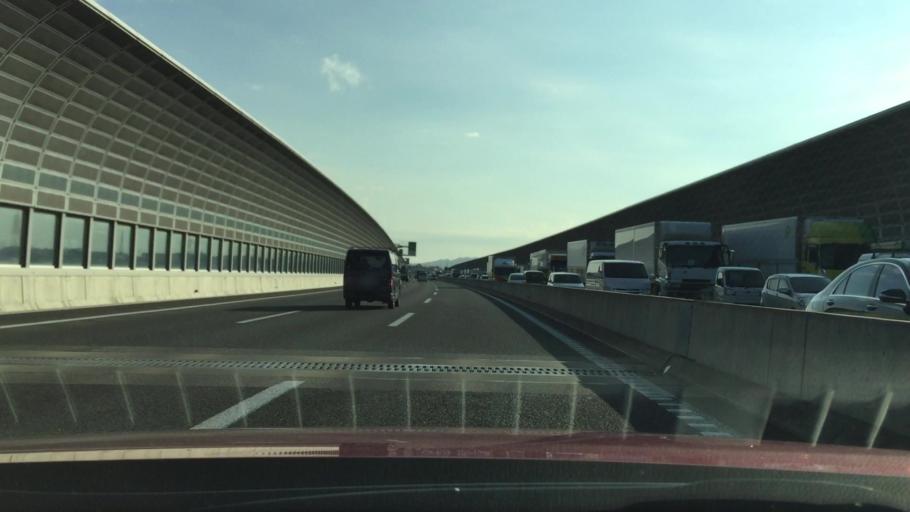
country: JP
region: Osaka
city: Neyagawa
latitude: 34.7472
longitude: 135.6272
